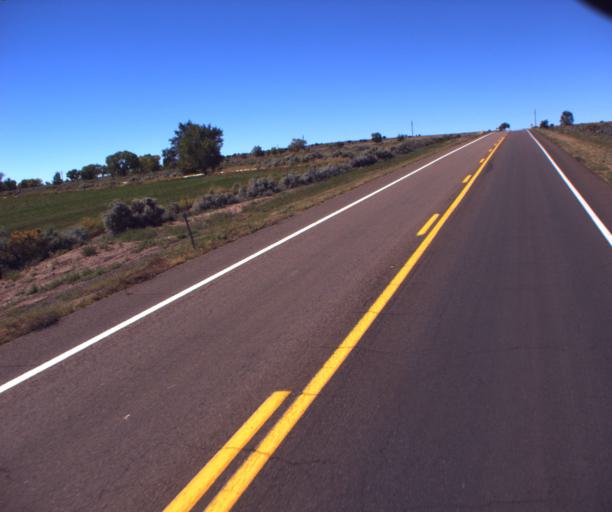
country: US
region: Arizona
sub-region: Apache County
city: Saint Johns
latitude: 34.5062
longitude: -109.4044
